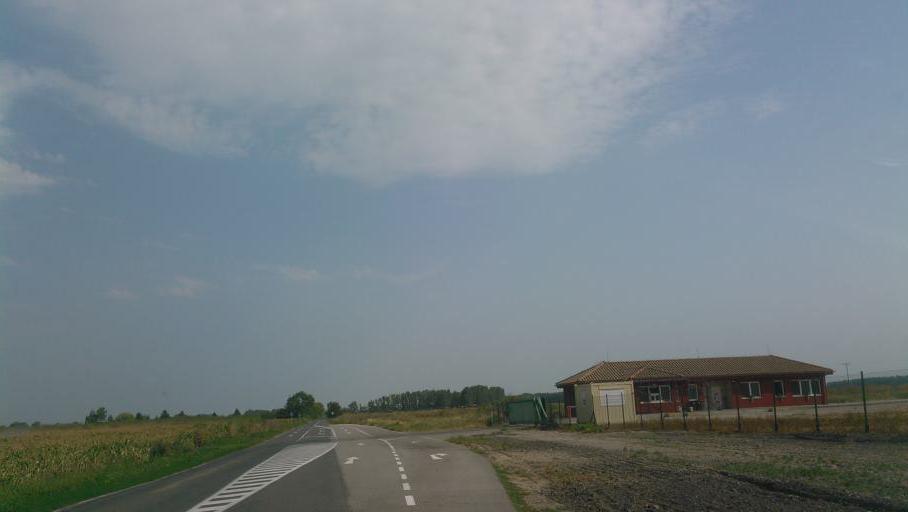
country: SK
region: Trnavsky
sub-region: Okres Dunajska Streda
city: Velky Meder
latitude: 47.9298
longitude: 17.7294
